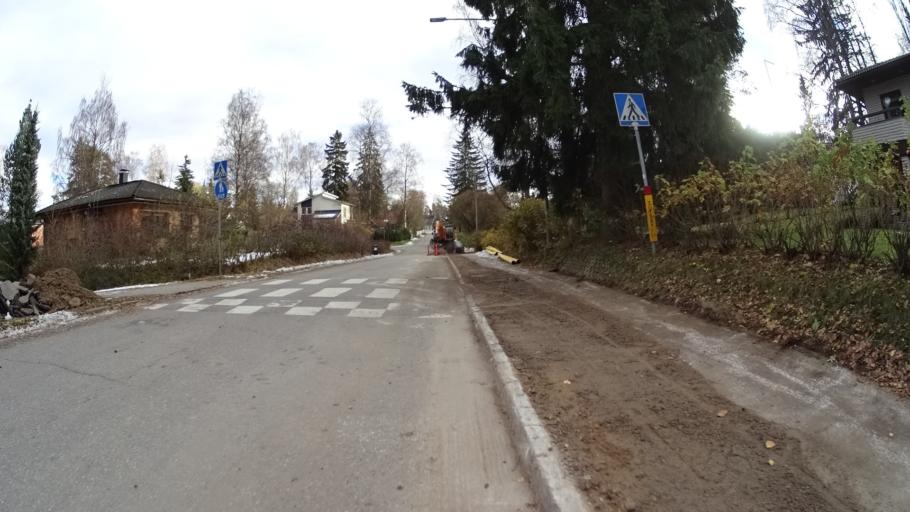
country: FI
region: Uusimaa
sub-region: Helsinki
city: Kilo
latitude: 60.2636
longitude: 24.8220
